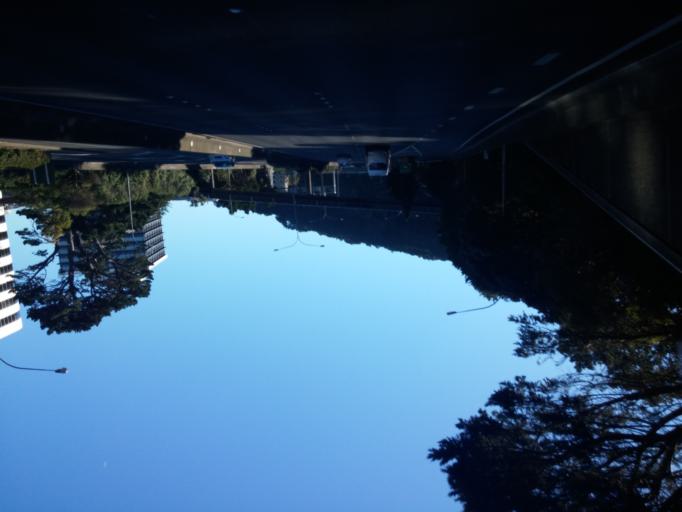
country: NZ
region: Wellington
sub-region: Wellington City
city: Wellington
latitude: -41.2798
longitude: 174.7734
